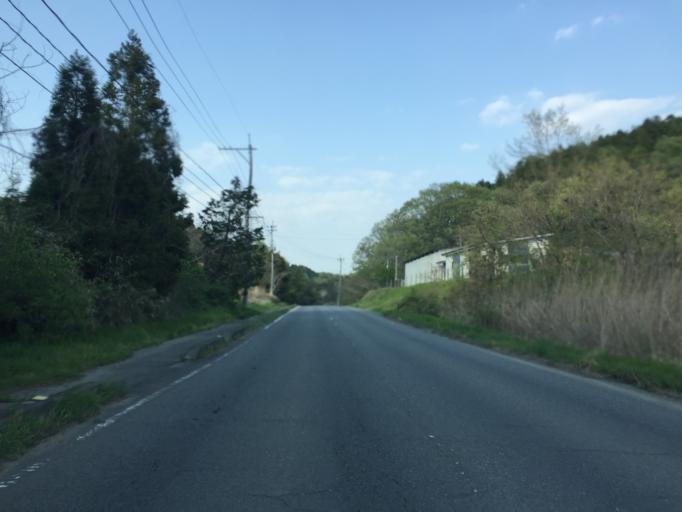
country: JP
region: Fukushima
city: Iwaki
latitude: 36.9726
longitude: 140.8390
